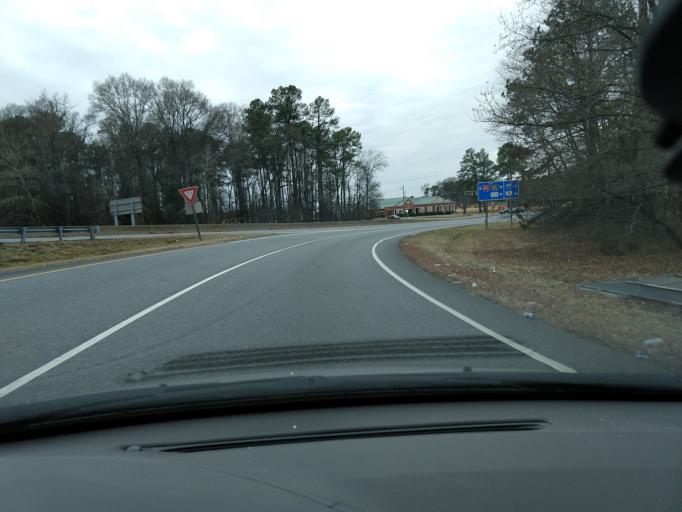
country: US
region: Virginia
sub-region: Chesterfield County
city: Bensley
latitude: 37.4644
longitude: -77.4263
